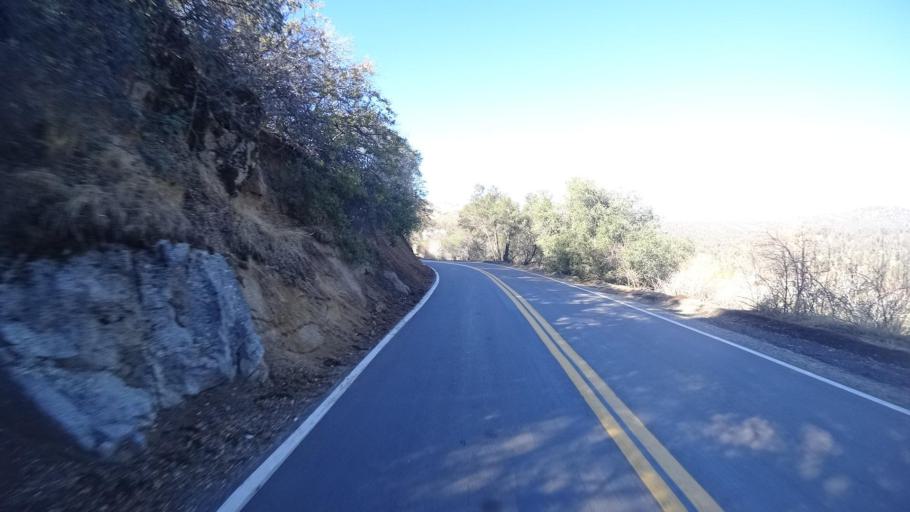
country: US
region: California
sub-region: Kern County
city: Alta Sierra
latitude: 35.7368
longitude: -118.6551
